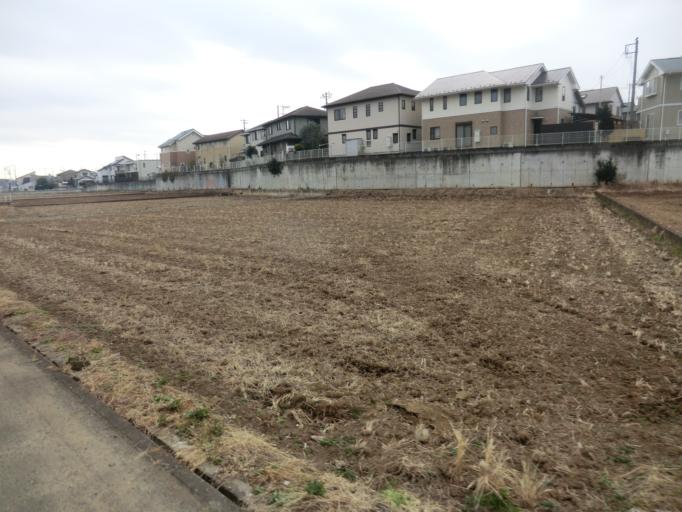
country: JP
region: Ibaraki
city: Naka
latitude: 36.0887
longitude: 140.1200
